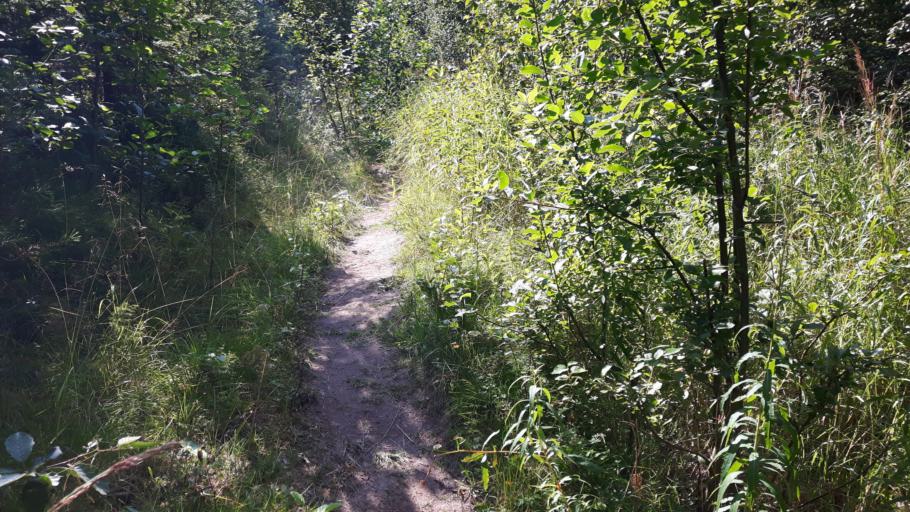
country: SE
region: Vaesternorrland
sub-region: Kramfors Kommun
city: Nordingra
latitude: 62.8294
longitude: 18.1663
